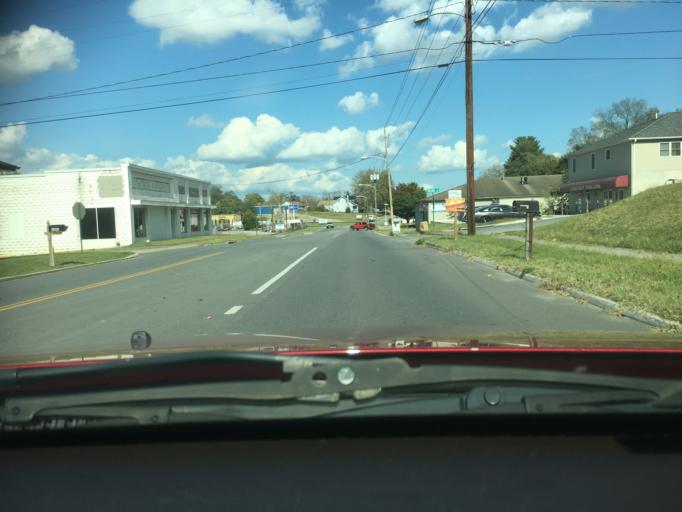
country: US
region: Virginia
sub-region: City of Radford
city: Radford
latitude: 37.1256
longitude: -80.5874
